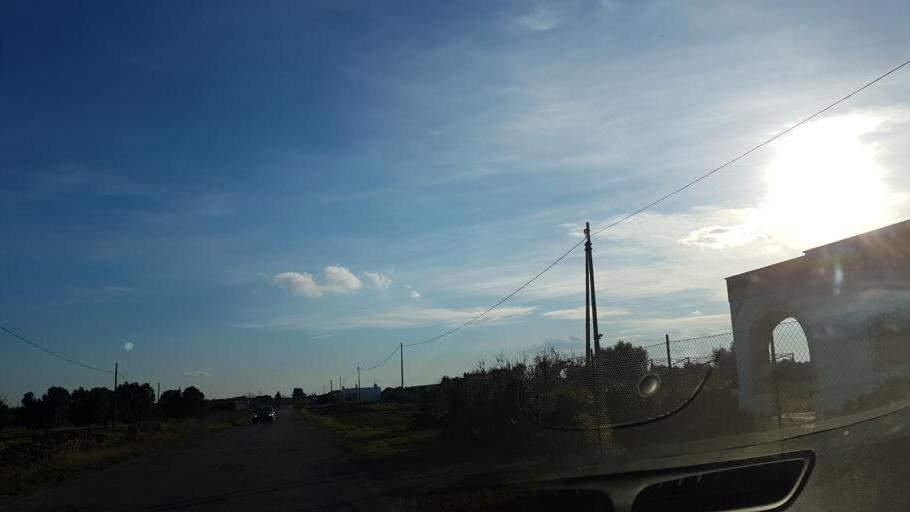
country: IT
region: Apulia
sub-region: Provincia di Brindisi
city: San Vito dei Normanni
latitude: 40.6669
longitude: 17.7800
